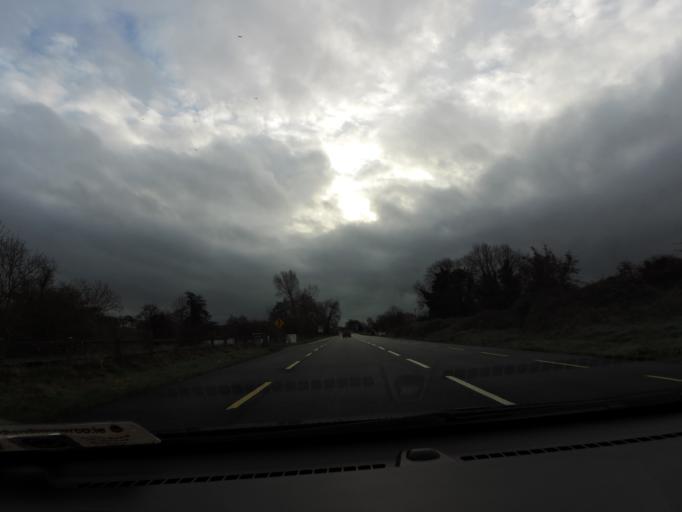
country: IE
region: Leinster
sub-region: Kilkenny
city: Ballyragget
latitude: 52.7899
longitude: -7.3449
